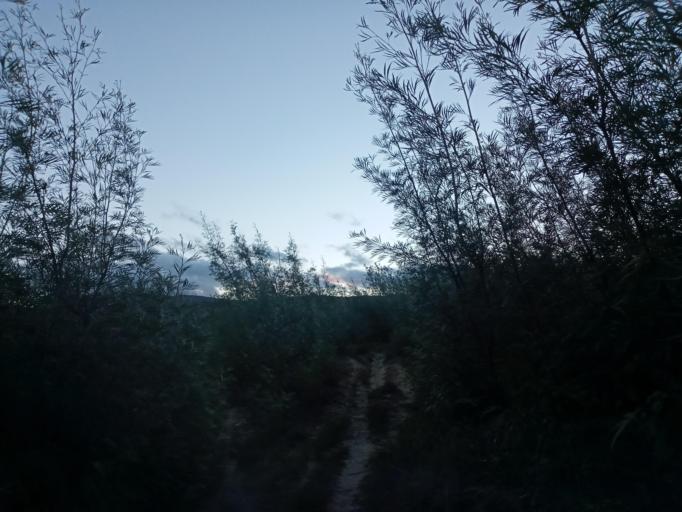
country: MG
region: Anosy
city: Fort Dauphin
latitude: -24.5115
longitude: 47.2233
